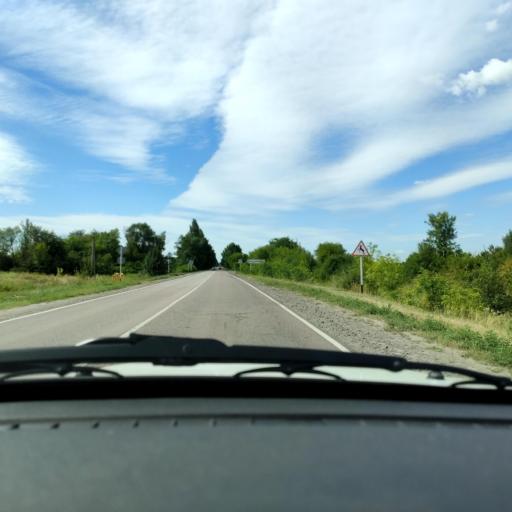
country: RU
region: Voronezj
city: Uglyanets
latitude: 51.8509
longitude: 39.6604
